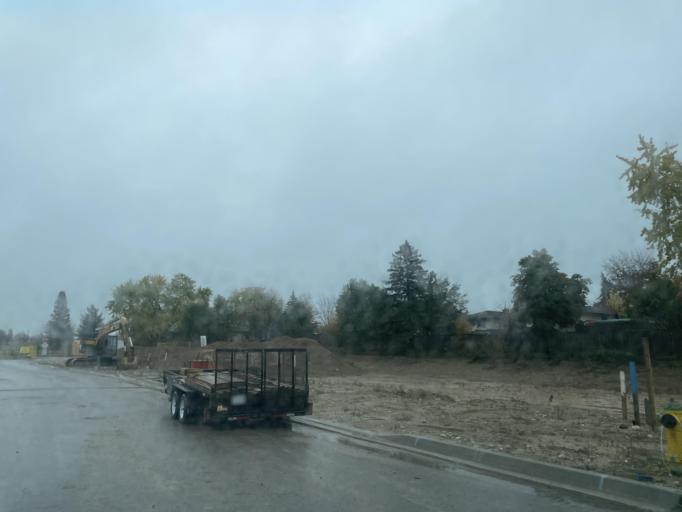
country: CA
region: Ontario
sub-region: Wellington County
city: Guelph
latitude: 43.5782
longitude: -80.2492
